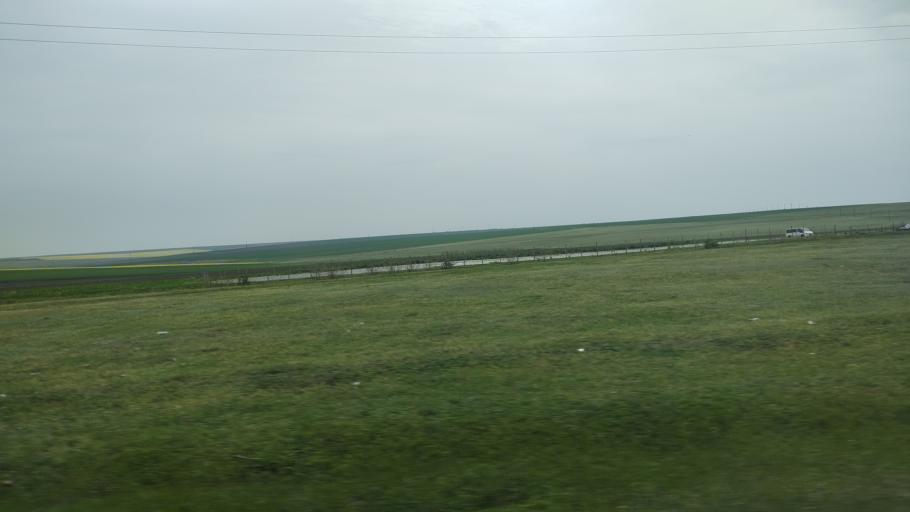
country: RO
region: Constanta
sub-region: Comuna Ciocarlia
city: Ciocarlia de Sus
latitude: 44.1254
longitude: 28.3387
